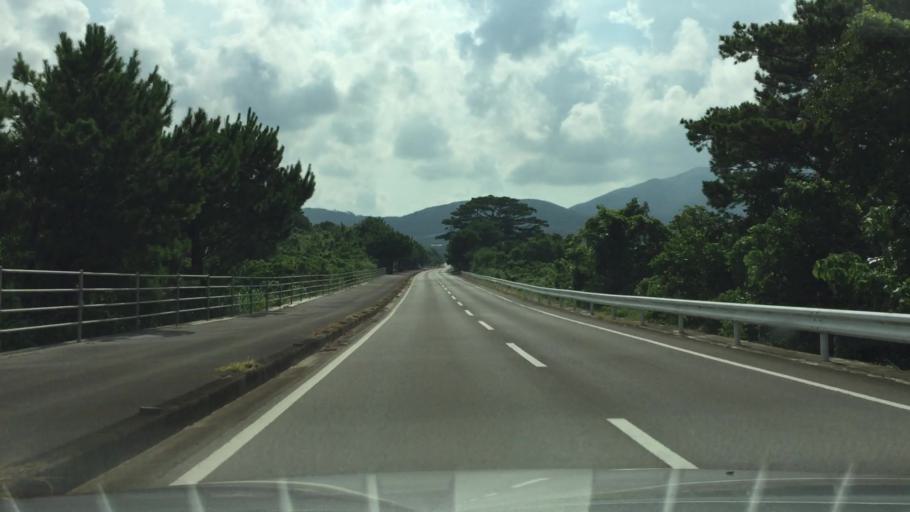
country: JP
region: Okinawa
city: Ishigaki
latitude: 24.4104
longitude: 124.2233
